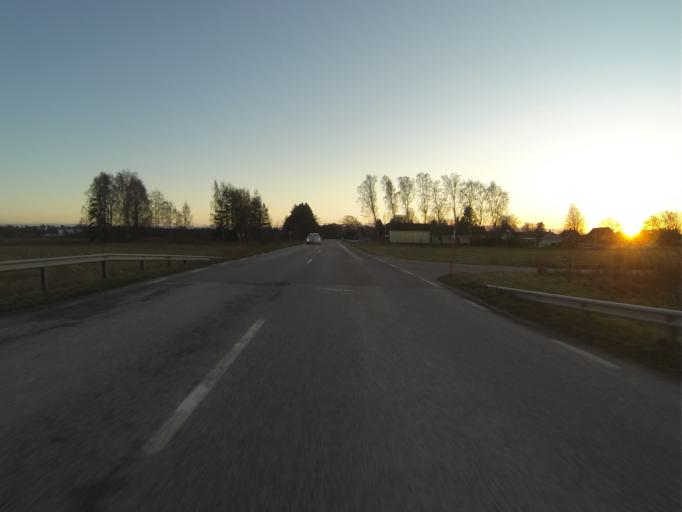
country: SE
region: Skane
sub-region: Hoors Kommun
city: Loberod
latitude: 55.7292
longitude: 13.4678
